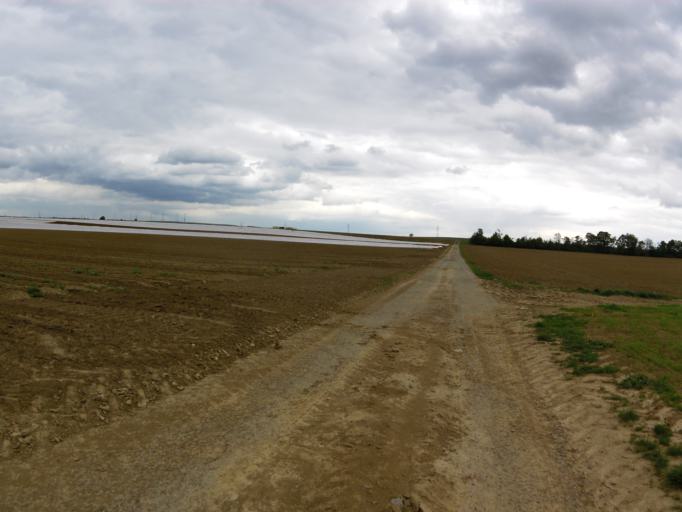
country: DE
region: Bavaria
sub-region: Regierungsbezirk Unterfranken
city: Unterpleichfeld
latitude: 49.8581
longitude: 10.0636
